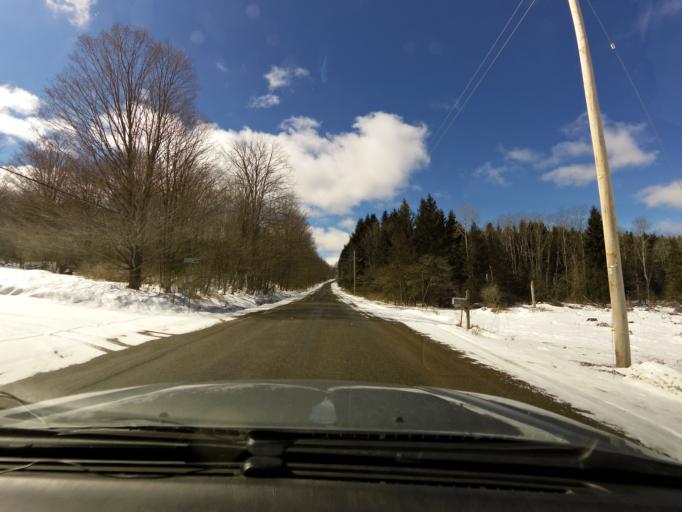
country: US
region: New York
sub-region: Cattaraugus County
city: Franklinville
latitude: 42.3654
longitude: -78.4126
